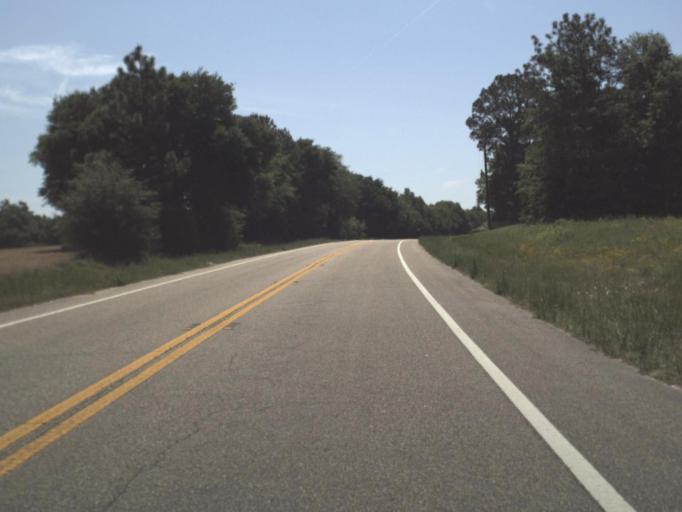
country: US
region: Florida
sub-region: Jackson County
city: Marianna
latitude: 30.6612
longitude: -85.2216
